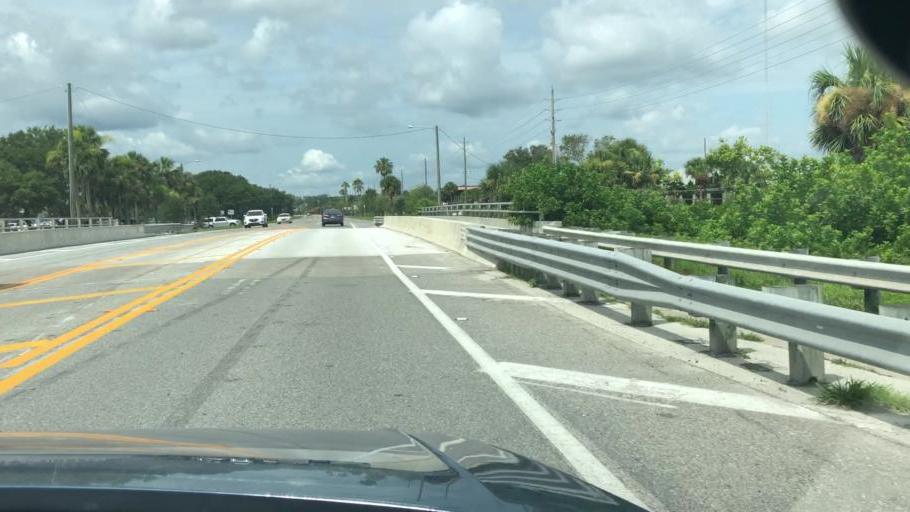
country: US
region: Florida
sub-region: Volusia County
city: New Smyrna Beach
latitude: 29.0328
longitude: -80.9163
